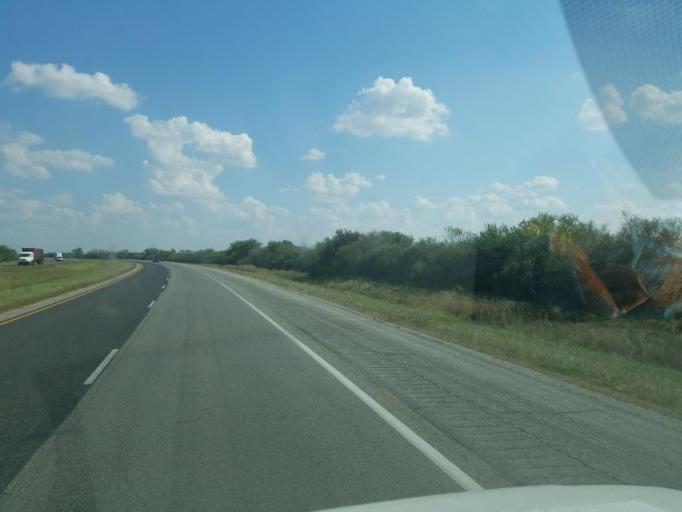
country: US
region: Indiana
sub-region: Allen County
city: Monroeville
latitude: 41.0020
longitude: -84.8302
